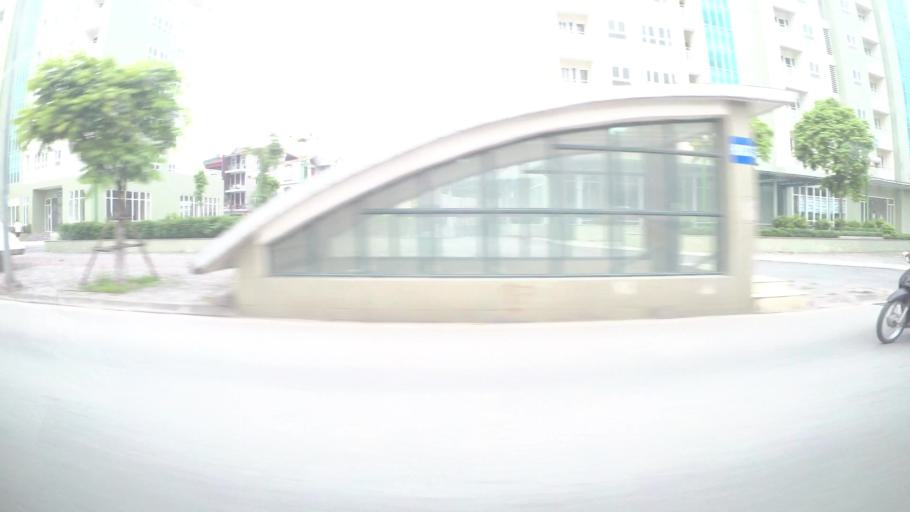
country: VN
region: Ha Noi
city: Hoan Kiem
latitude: 21.0590
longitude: 105.8841
